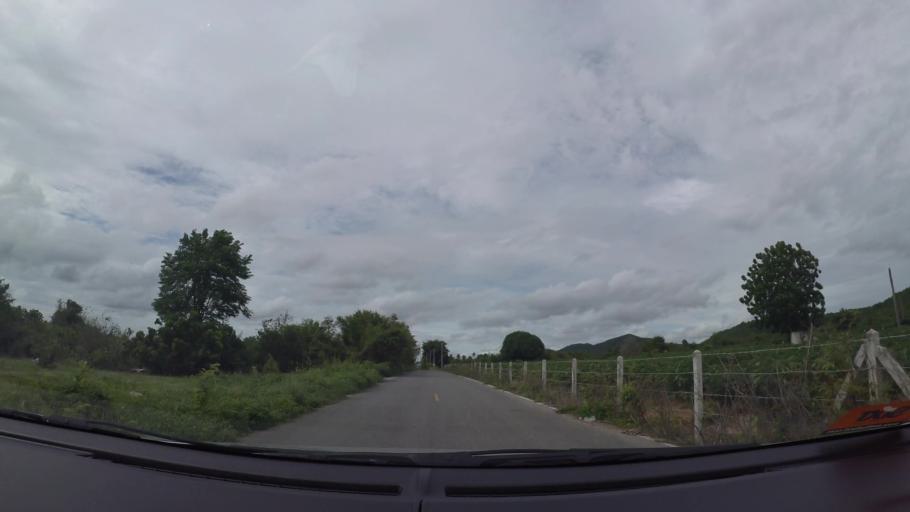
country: TH
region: Chon Buri
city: Sattahip
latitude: 12.7092
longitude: 100.9012
